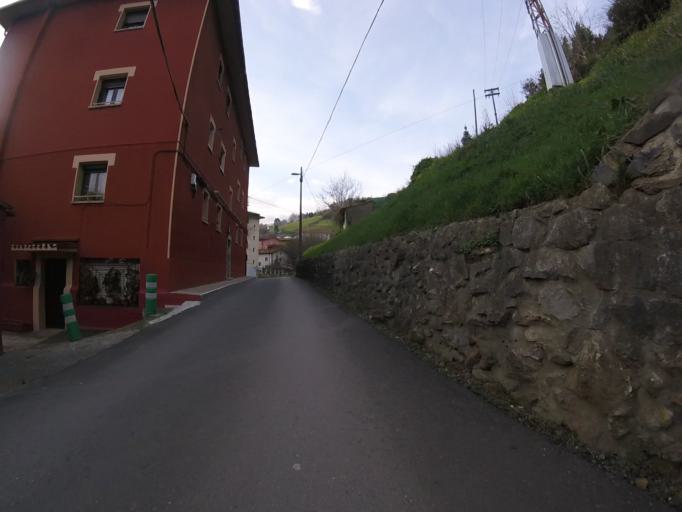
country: ES
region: Basque Country
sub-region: Provincia de Guipuzcoa
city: Anoeta
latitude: 43.1648
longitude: -2.0719
